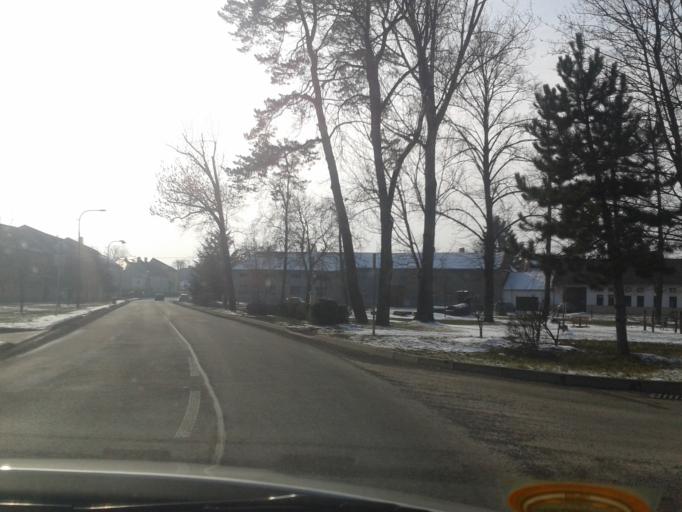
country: CZ
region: Olomoucky
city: Smrzice
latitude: 49.5067
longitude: 17.1020
